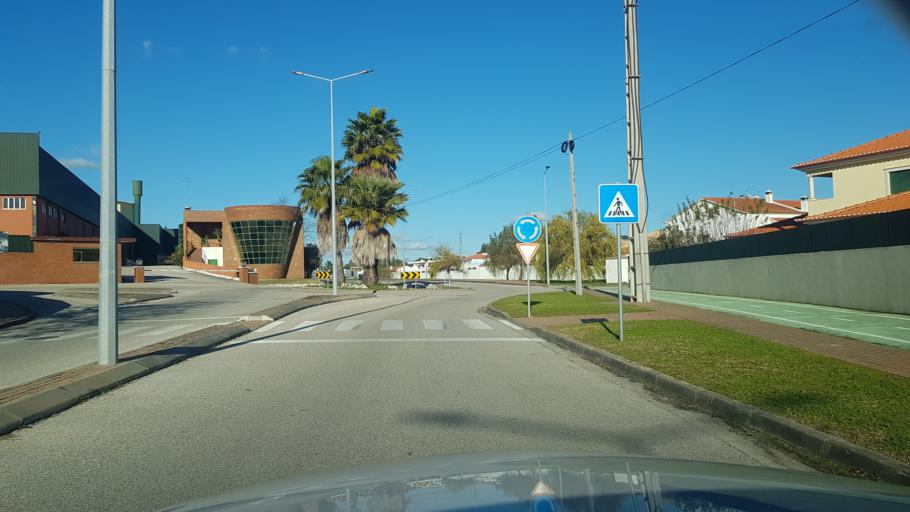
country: PT
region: Santarem
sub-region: Entroncamento
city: Entroncamento
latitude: 39.4812
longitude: -8.4723
